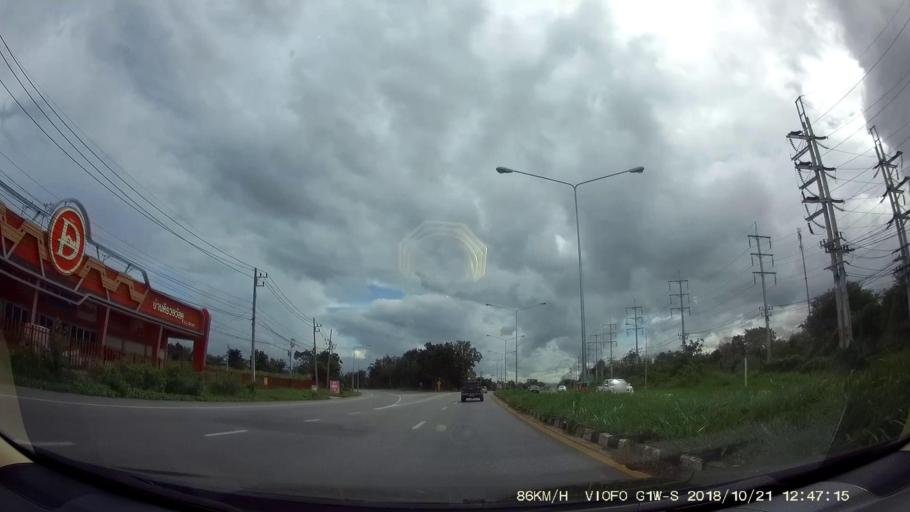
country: TH
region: Nakhon Ratchasima
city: Amphoe Sikhiu
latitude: 14.9310
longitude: 101.6833
